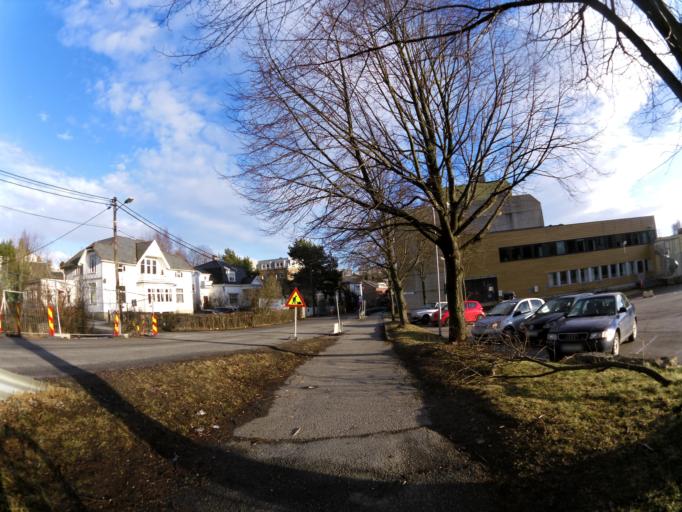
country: NO
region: Ostfold
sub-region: Fredrikstad
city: Fredrikstad
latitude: 59.2196
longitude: 10.9426
